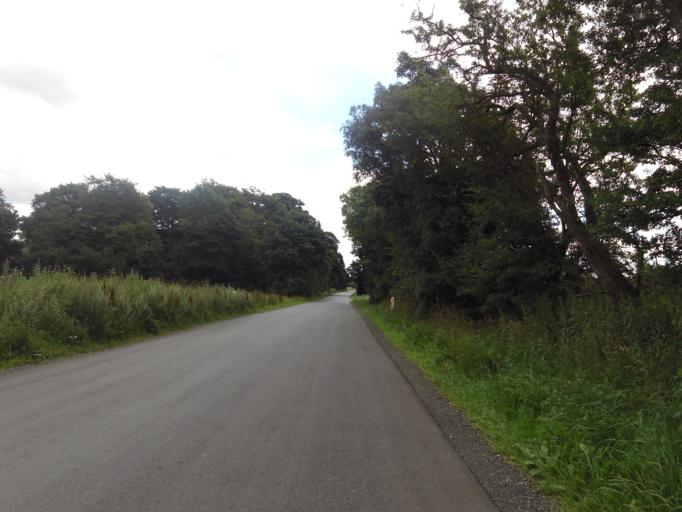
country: DK
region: South Denmark
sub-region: Haderslev Kommune
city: Vojens
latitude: 55.2750
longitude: 9.2685
